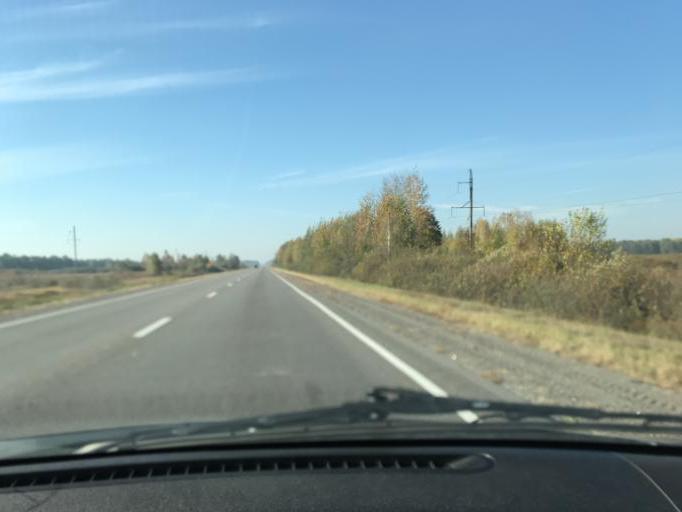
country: BY
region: Brest
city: Horad Luninyets
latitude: 52.3101
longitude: 26.5299
